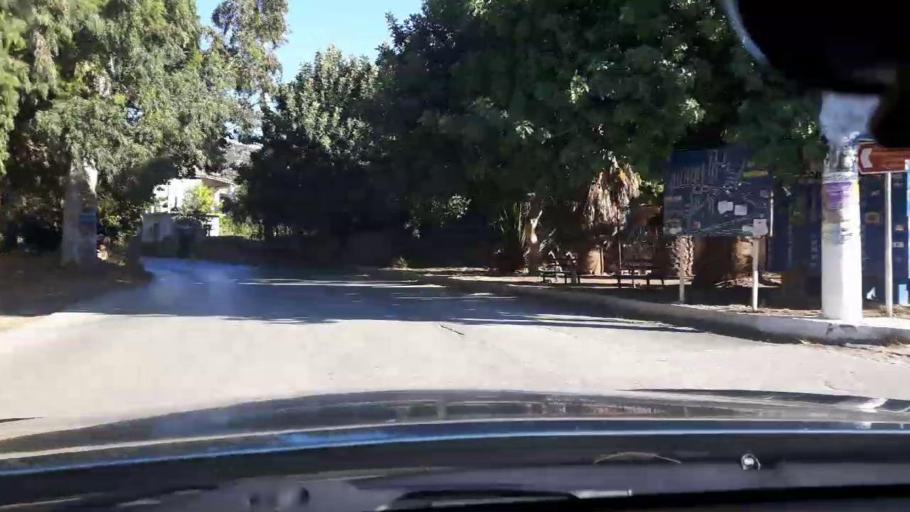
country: GR
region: Attica
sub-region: Nomarchia Anatolikis Attikis
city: Limin Mesoyaias
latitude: 37.8684
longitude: 24.0196
